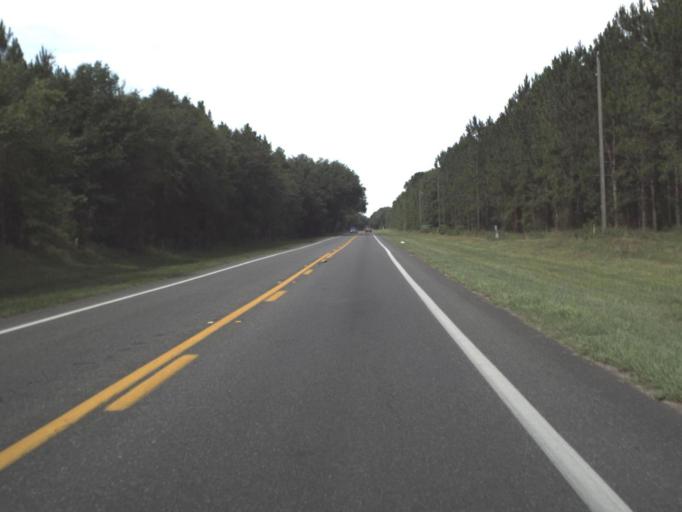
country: US
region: Florida
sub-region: Suwannee County
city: Live Oak
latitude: 30.2733
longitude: -83.0154
